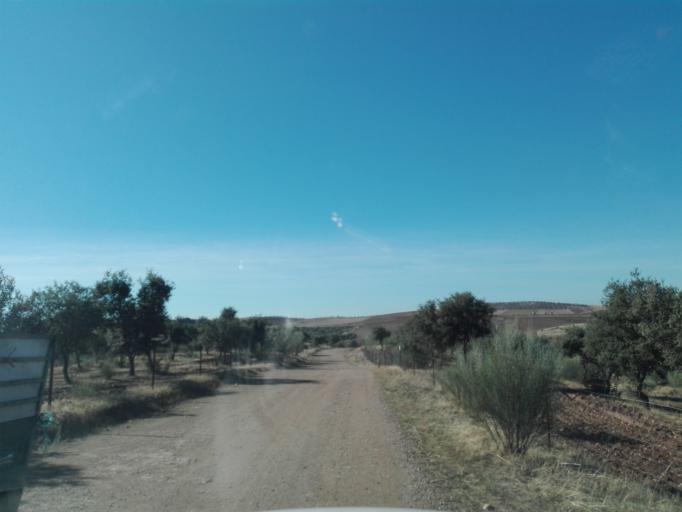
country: ES
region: Extremadura
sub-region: Provincia de Badajoz
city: Llera
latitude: 38.4462
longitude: -6.0428
